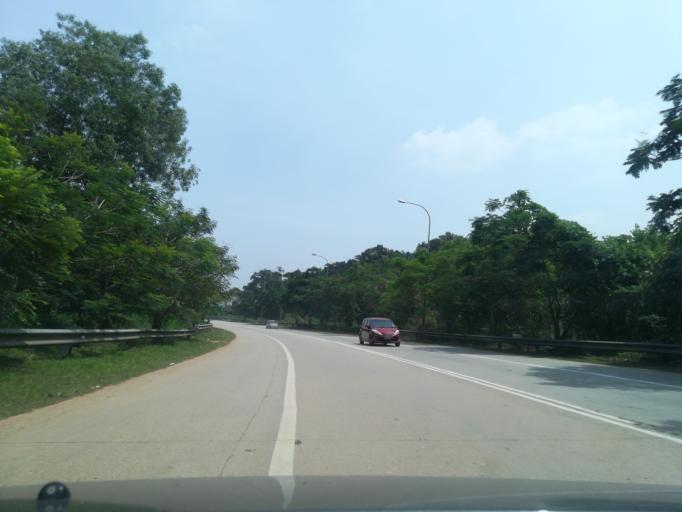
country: MY
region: Kedah
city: Kulim
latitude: 5.4274
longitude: 100.5630
